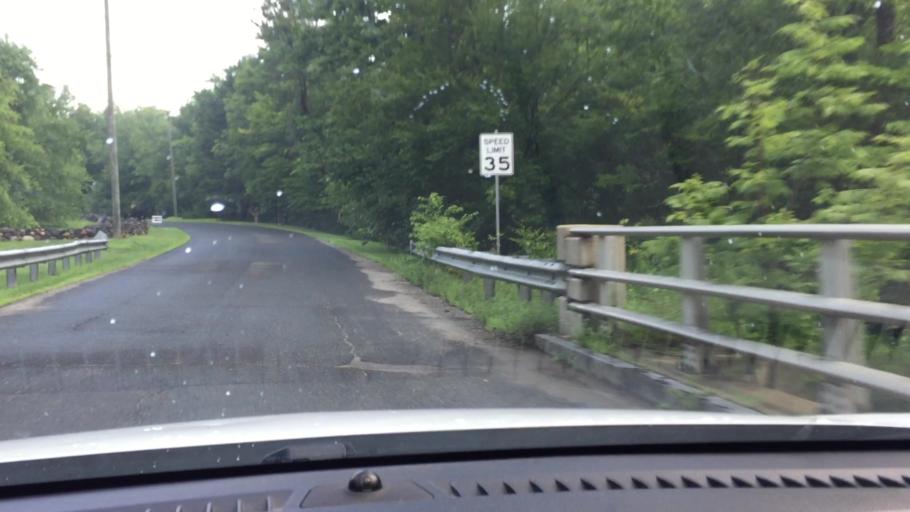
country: US
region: Massachusetts
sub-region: Berkshire County
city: Becket
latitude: 42.3519
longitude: -72.9616
